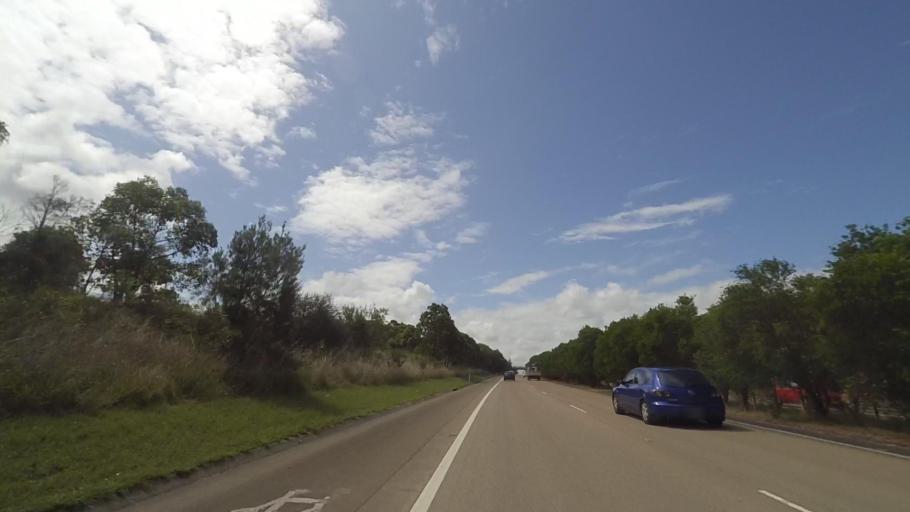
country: AU
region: New South Wales
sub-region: Lake Macquarie Shire
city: Gateshead
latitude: -32.9796
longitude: 151.6798
